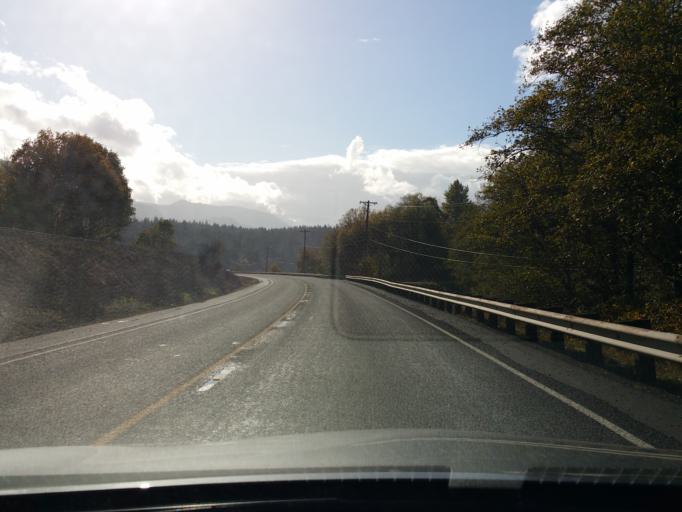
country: US
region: Oregon
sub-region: Hood River County
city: Cascade Locks
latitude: 45.6792
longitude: -121.9067
